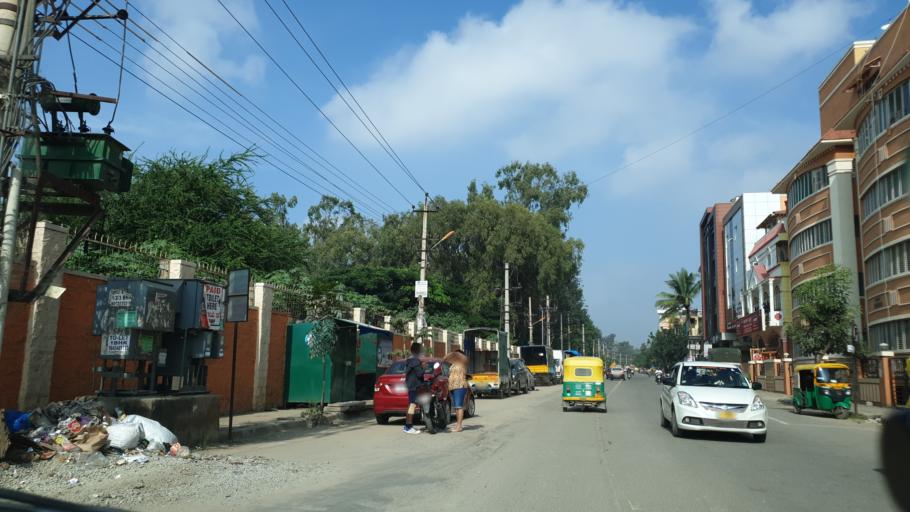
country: IN
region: Karnataka
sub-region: Bangalore Urban
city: Bangalore
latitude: 12.9728
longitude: 77.6776
